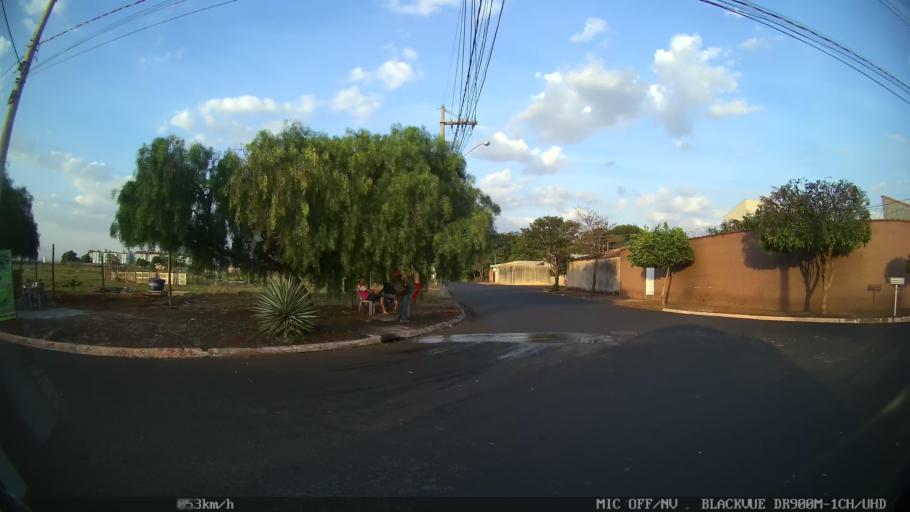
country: BR
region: Sao Paulo
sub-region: Ribeirao Preto
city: Ribeirao Preto
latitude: -21.1378
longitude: -47.8574
